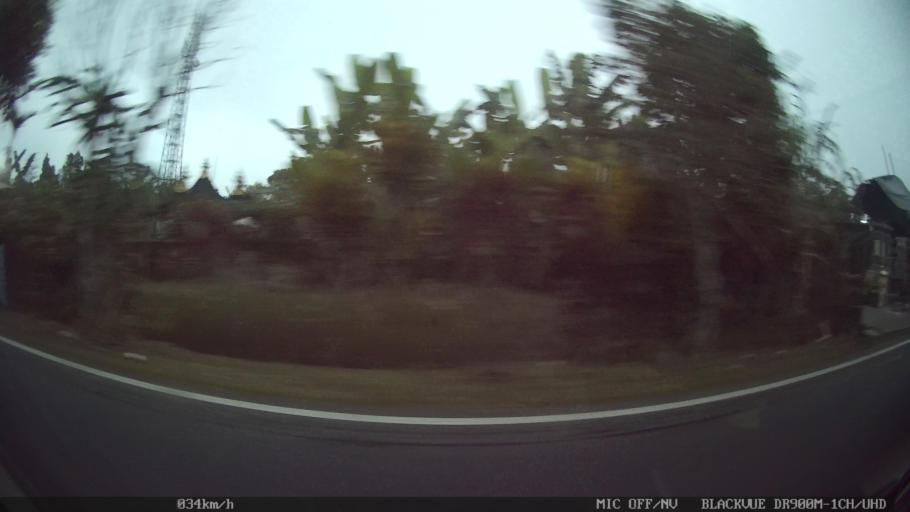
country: ID
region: Bali
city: Banjar Taro Kelod
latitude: -8.3119
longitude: 115.3030
